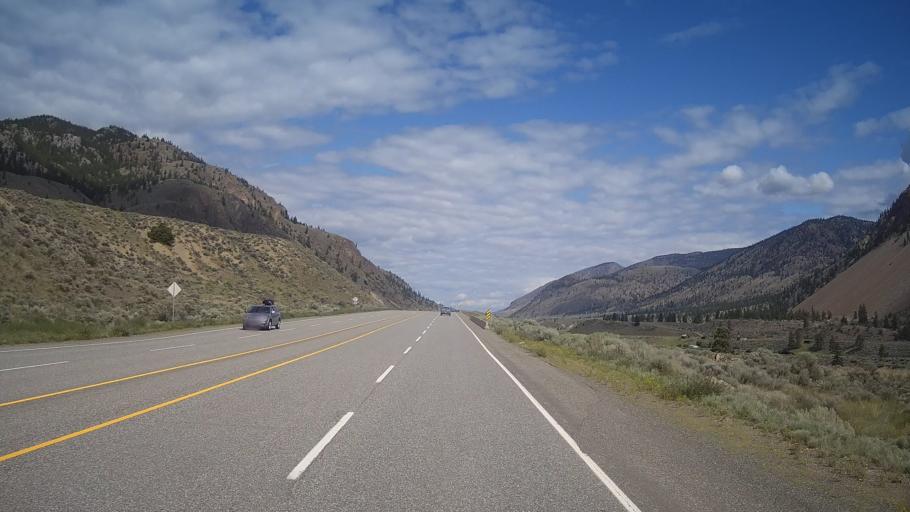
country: CA
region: British Columbia
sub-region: Thompson-Nicola Regional District
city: Ashcroft
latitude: 50.5135
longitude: -121.2811
